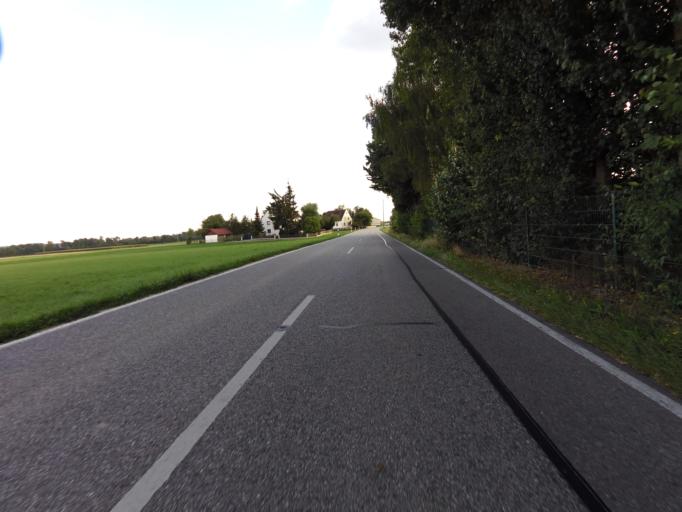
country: DE
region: Bavaria
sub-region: Upper Bavaria
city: Wang
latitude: 48.4851
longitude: 11.9611
